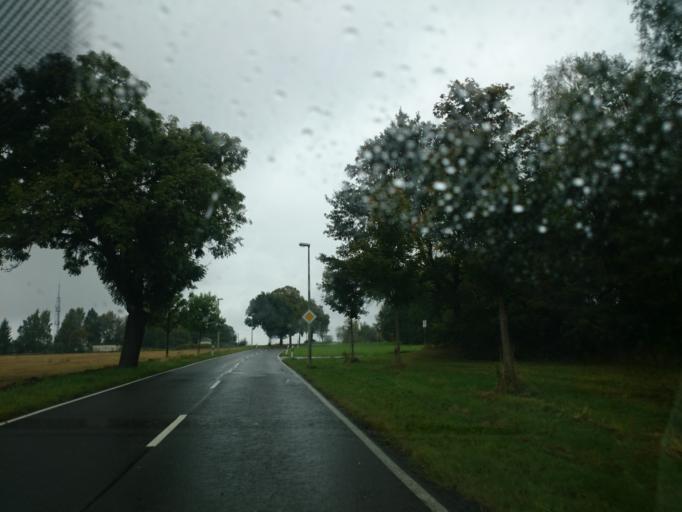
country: DE
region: Saxony
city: Brand-Erbisdorf
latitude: 50.8799
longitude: 13.3383
